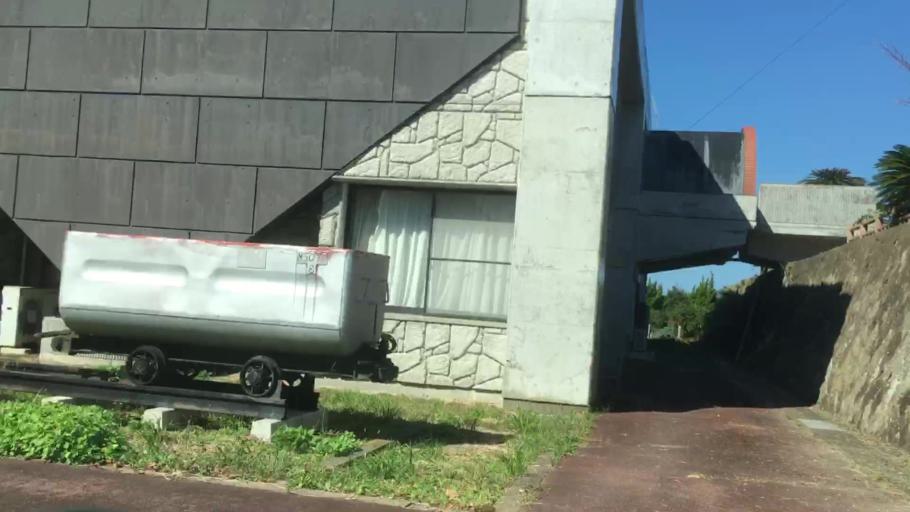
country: JP
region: Nagasaki
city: Sasebo
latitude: 33.0196
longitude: 129.5747
